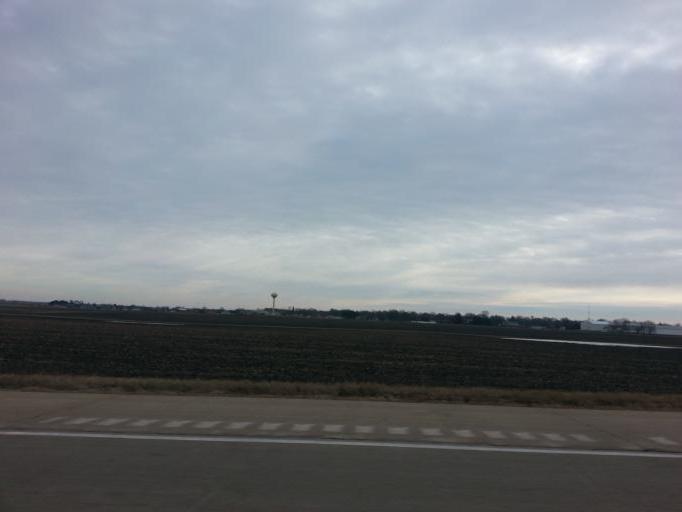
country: US
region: Illinois
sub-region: Woodford County
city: El Paso
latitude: 40.7424
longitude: -89.0344
